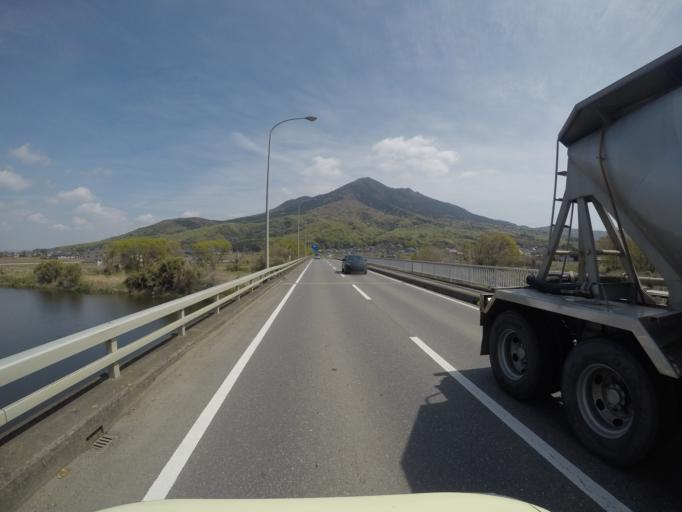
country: JP
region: Ibaraki
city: Tsukuba
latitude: 36.2060
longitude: 140.0720
